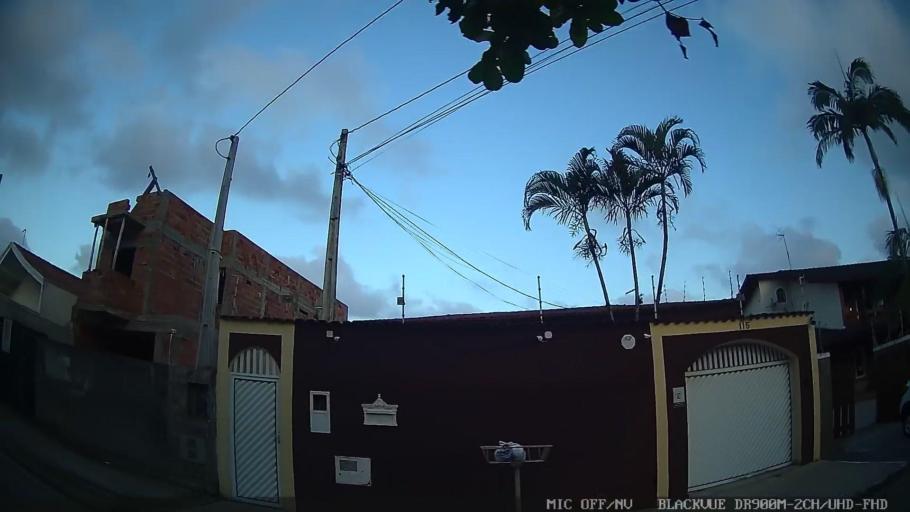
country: BR
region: Sao Paulo
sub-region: Peruibe
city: Peruibe
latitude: -24.3234
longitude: -47.0020
